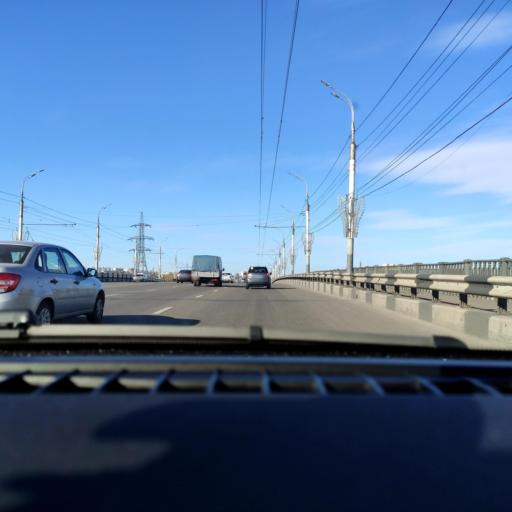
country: RU
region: Voronezj
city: Voronezh
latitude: 51.6327
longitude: 39.2232
